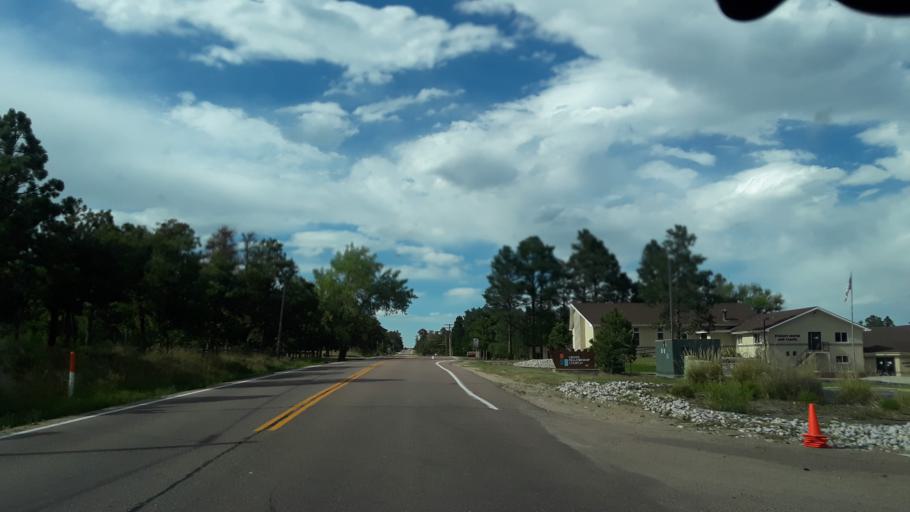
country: US
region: Colorado
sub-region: El Paso County
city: Black Forest
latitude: 38.9888
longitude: -104.7003
